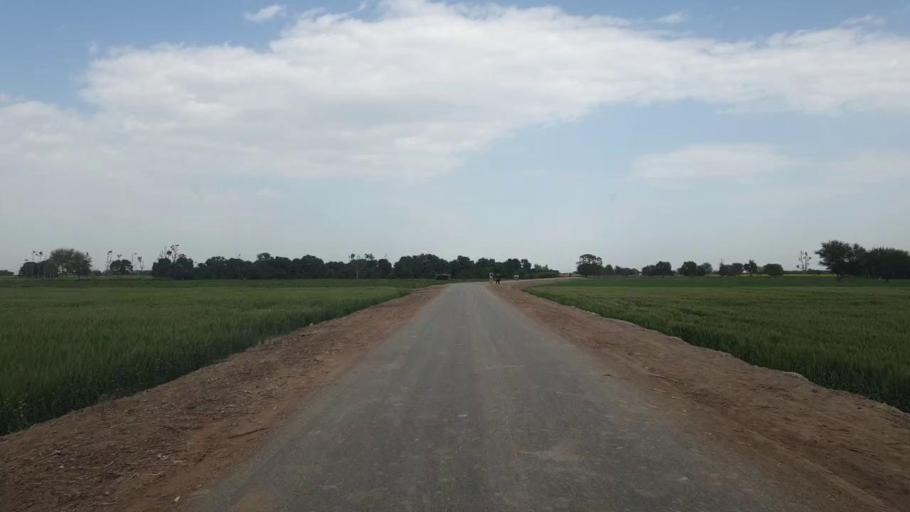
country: PK
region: Sindh
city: Hala
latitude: 25.9642
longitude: 68.3954
